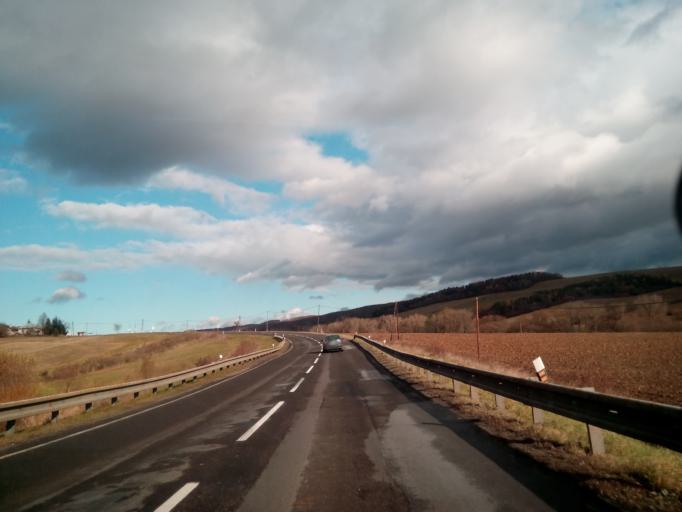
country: SK
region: Presovsky
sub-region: Okres Bardejov
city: Bardejov
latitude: 49.1840
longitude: 21.3092
